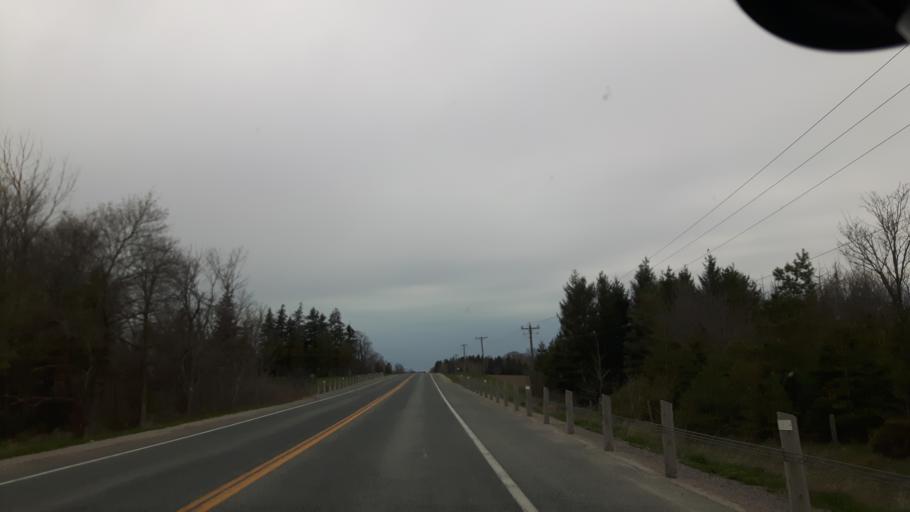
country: CA
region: Ontario
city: Bluewater
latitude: 43.6239
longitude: -81.5554
